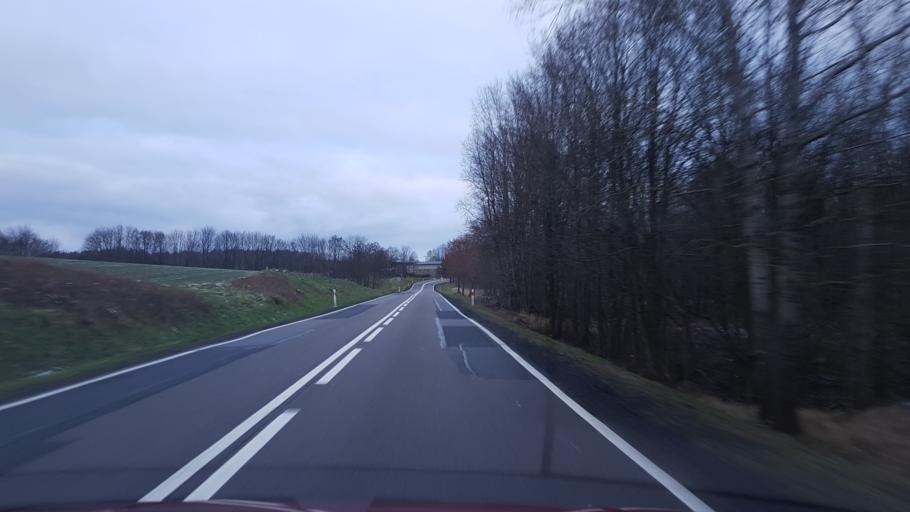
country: PL
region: Pomeranian Voivodeship
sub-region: Powiat bytowski
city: Tuchomie
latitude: 54.0644
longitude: 17.2568
